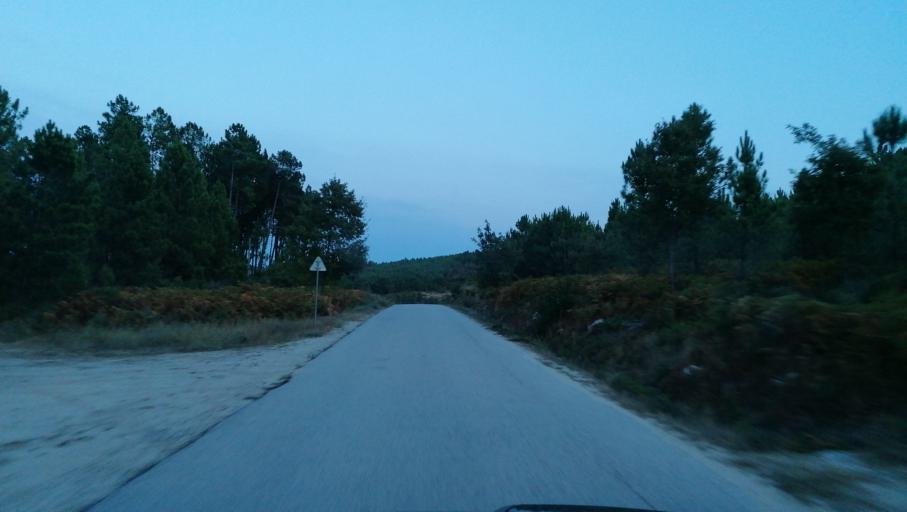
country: PT
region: Vila Real
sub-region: Vila Pouca de Aguiar
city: Vila Pouca de Aguiar
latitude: 41.5564
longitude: -7.6396
